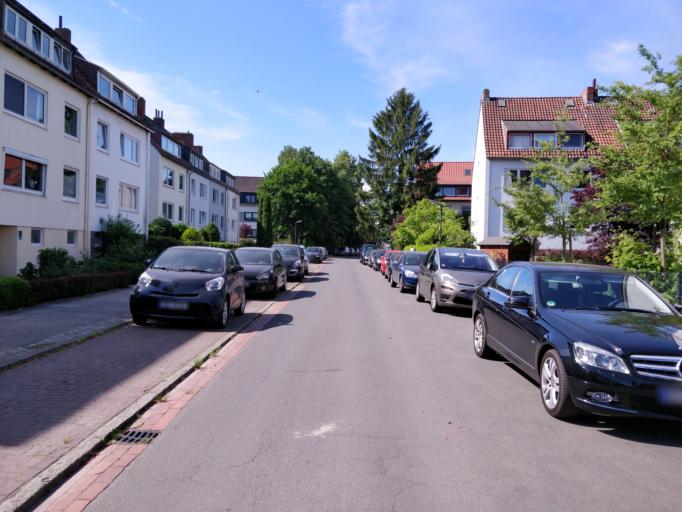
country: DE
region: Lower Saxony
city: Lilienthal
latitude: 53.1032
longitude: 8.8758
